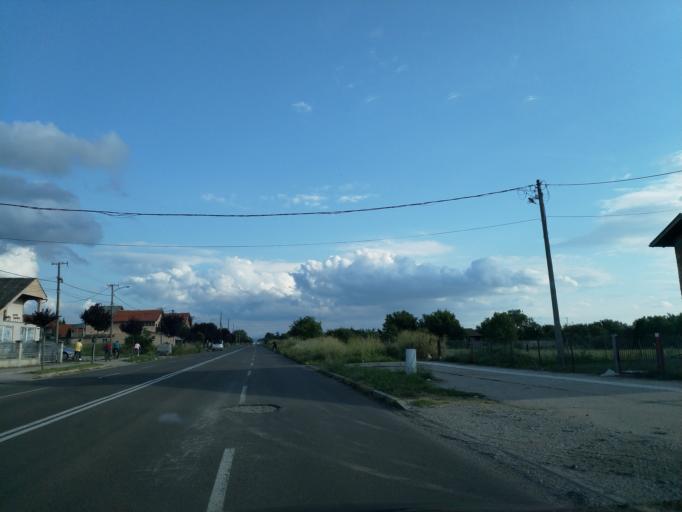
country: RS
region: Central Serbia
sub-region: Pomoravski Okrug
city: Paracin
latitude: 43.8411
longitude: 21.4150
